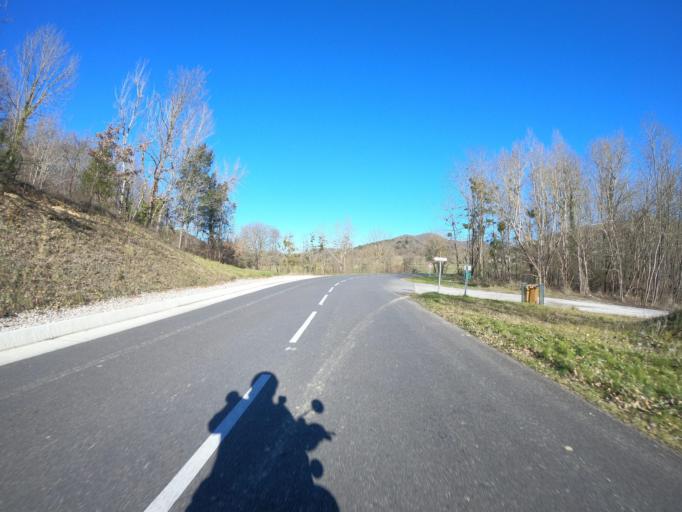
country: FR
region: Midi-Pyrenees
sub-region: Departement de l'Ariege
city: Mirepoix
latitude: 43.0861
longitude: 1.8081
